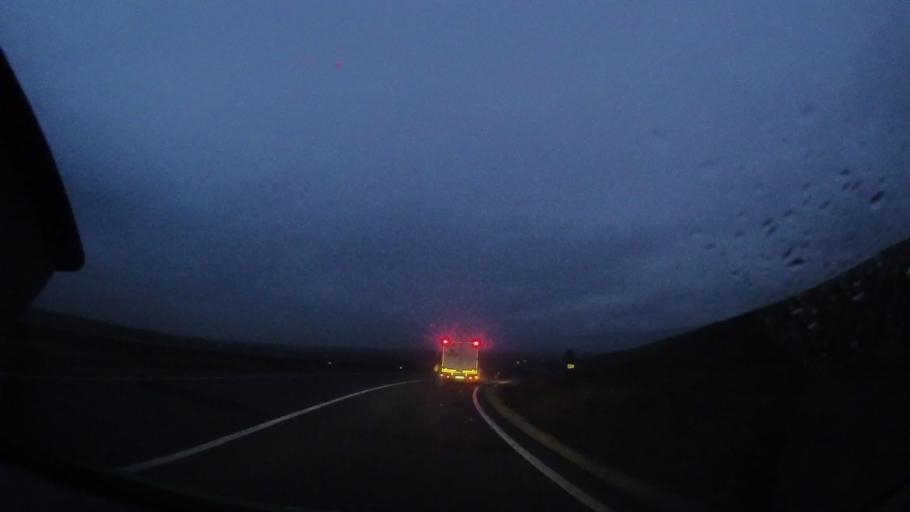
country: RO
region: Harghita
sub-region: Comuna Subcetate
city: Subcetate
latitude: 46.8504
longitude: 25.4681
